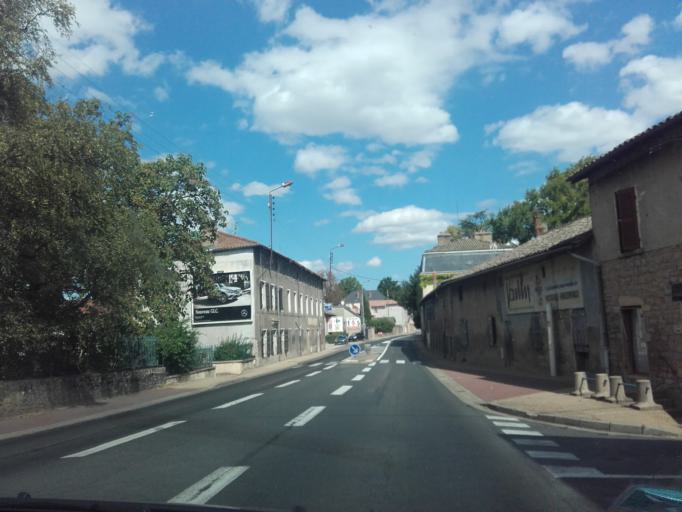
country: FR
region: Bourgogne
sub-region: Departement de Saone-et-Loire
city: La Chapelle-de-Guinchay
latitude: 46.2068
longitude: 4.7705
